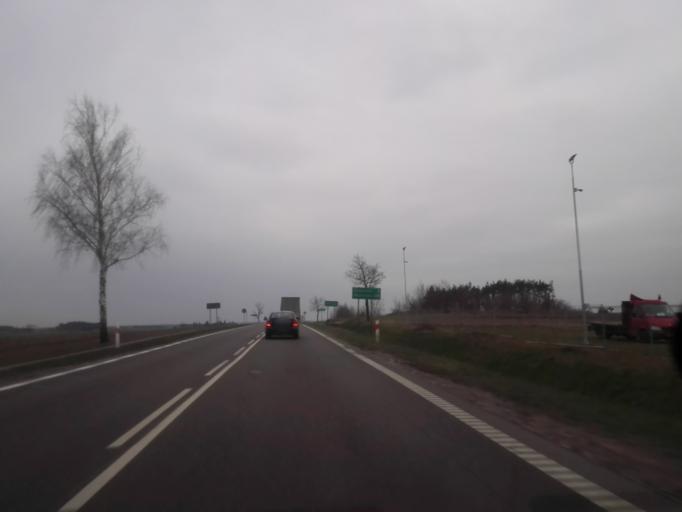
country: PL
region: Podlasie
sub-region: Powiat grajewski
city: Szczuczyn
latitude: 53.5856
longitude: 22.3273
